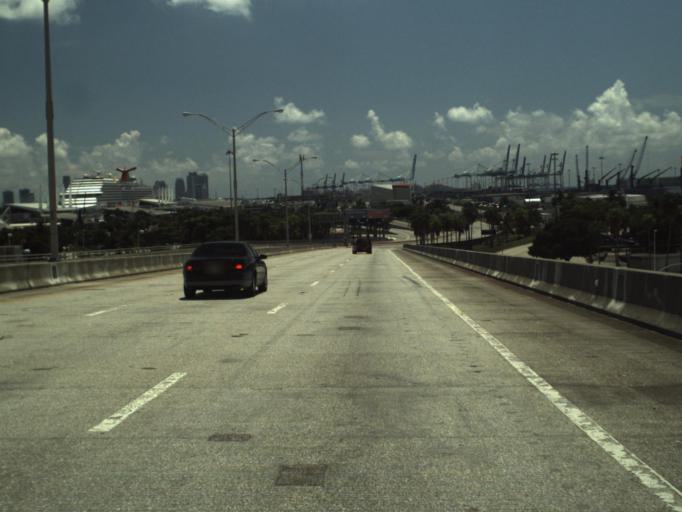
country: US
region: Florida
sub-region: Miami-Dade County
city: Miami
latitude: 25.7787
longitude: -80.1804
